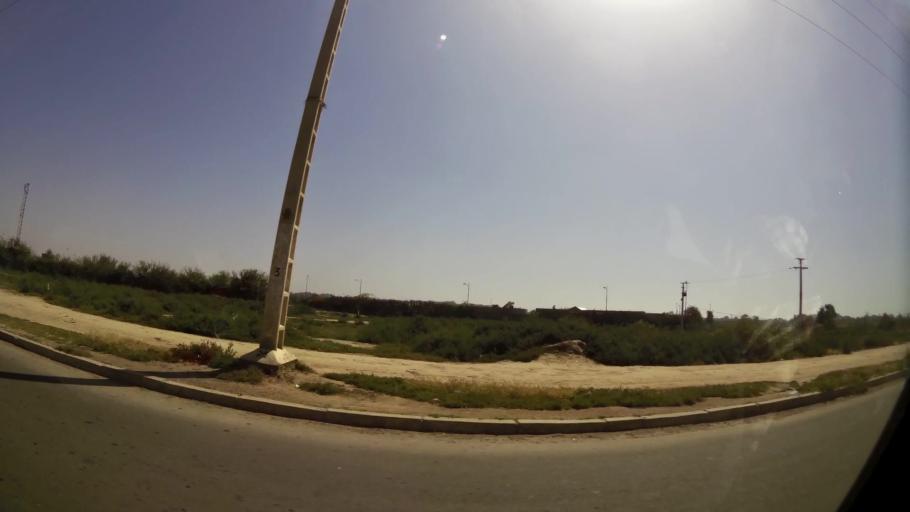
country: MA
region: Souss-Massa-Draa
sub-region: Inezgane-Ait Mellou
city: Inezgane
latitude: 30.3563
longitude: -9.5635
